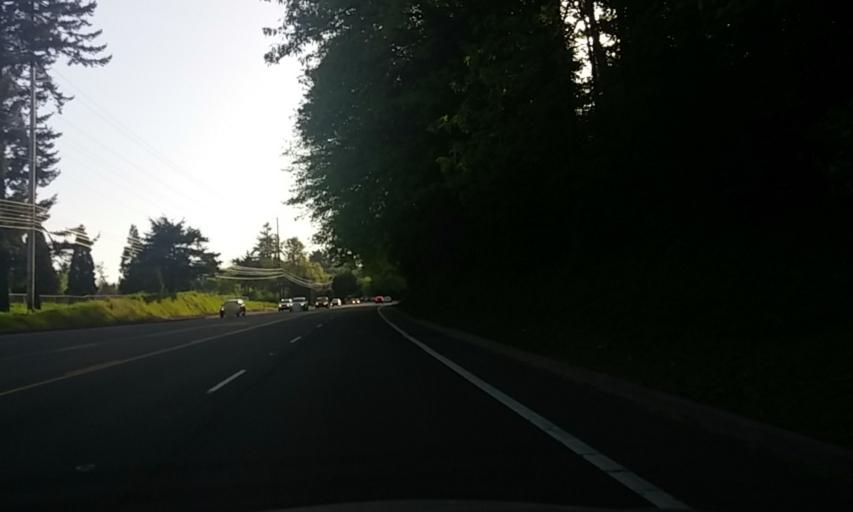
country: US
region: Oregon
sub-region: Washington County
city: Metzger
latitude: 45.4444
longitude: -122.7361
